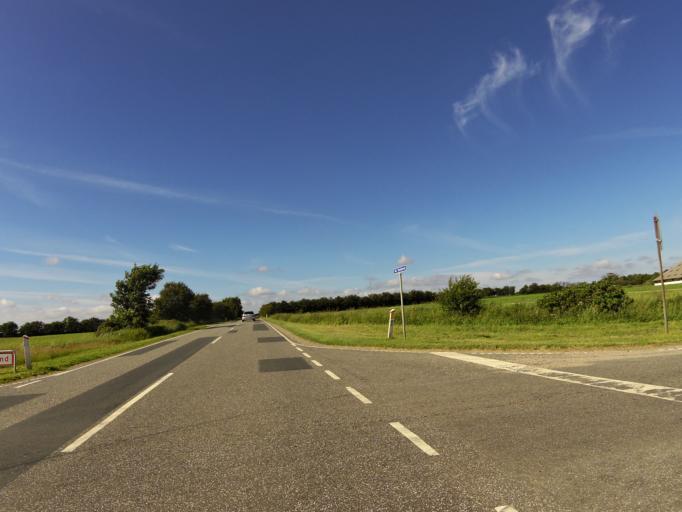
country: DK
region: South Denmark
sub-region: Tonder Kommune
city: Toftlund
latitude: 55.0972
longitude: 9.1751
